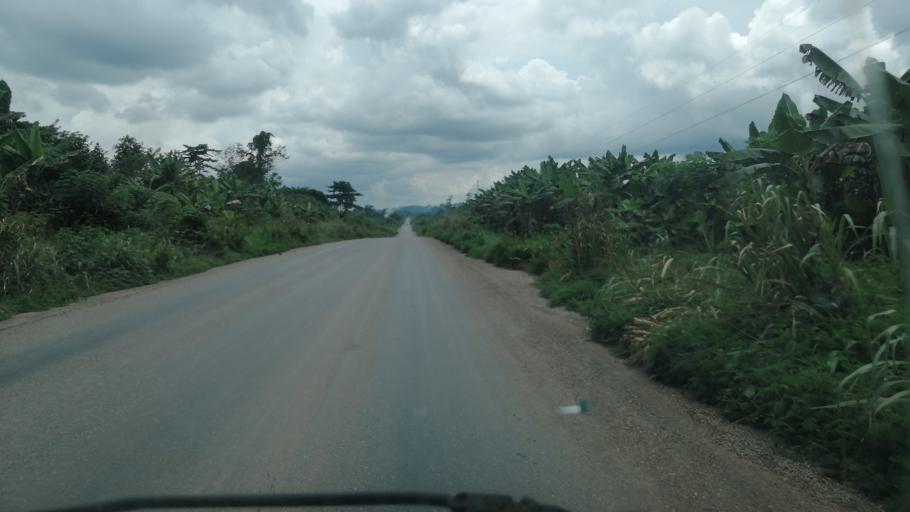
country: GH
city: Duayaw Nkwanta
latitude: 6.9072
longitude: -2.3961
